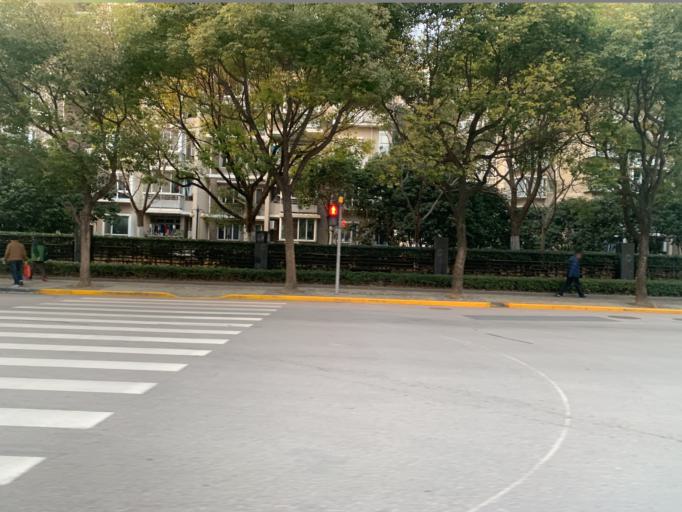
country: CN
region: Shanghai Shi
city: Huamu
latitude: 31.2281
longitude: 121.5477
